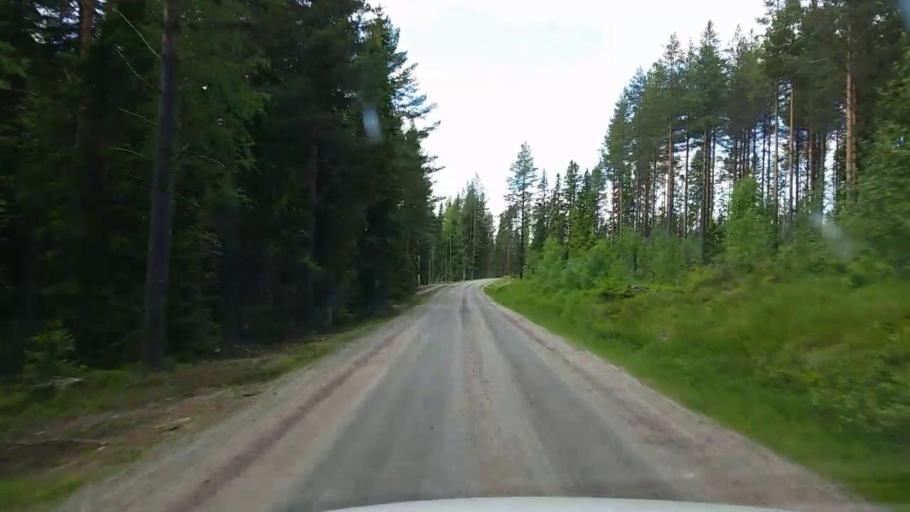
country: SE
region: Gaevleborg
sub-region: Ovanakers Kommun
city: Edsbyn
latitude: 61.5660
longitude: 15.9572
